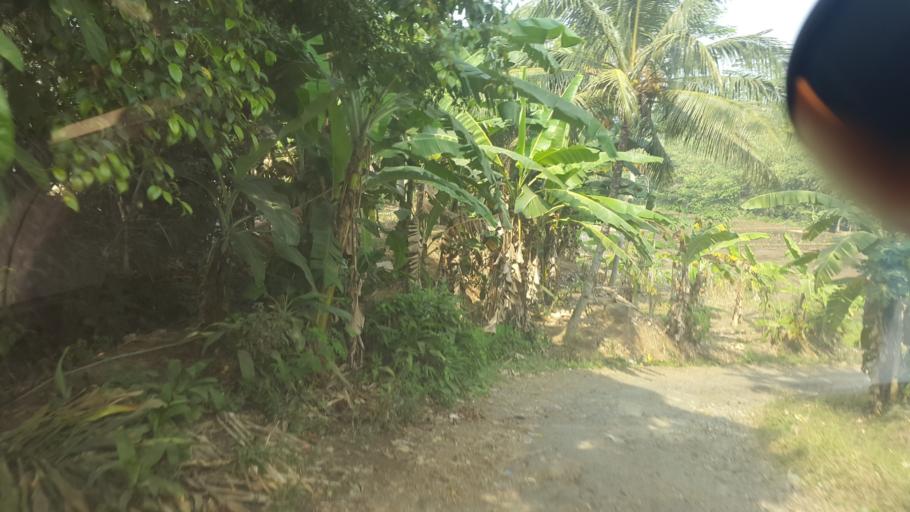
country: ID
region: West Java
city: Cilandak
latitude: -6.9979
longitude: 106.7551
